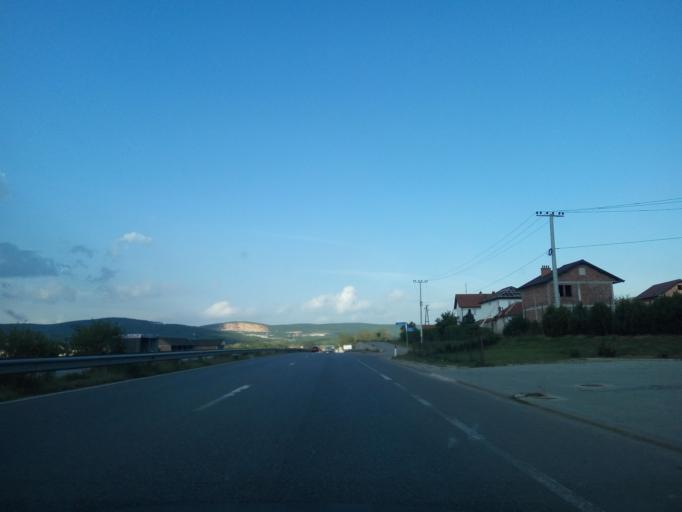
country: XK
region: Pristina
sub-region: Komuna e Drenasit
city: Glogovac
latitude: 42.5963
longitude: 20.9308
